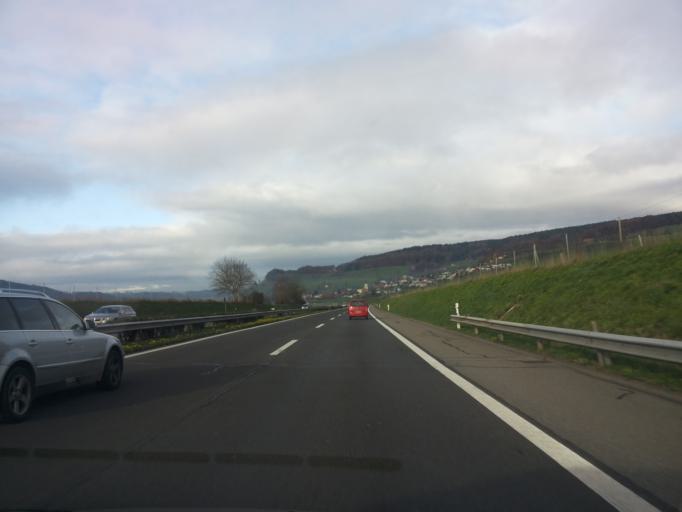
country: CH
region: Lucerne
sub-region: Willisau District
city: Wauwil
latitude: 47.2047
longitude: 8.0393
